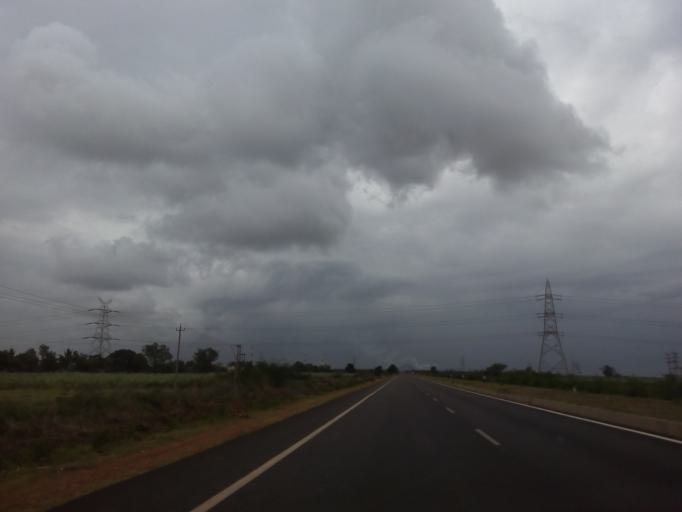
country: IN
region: Karnataka
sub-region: Davanagere
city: Harihar
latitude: 14.5436
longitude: 75.7510
